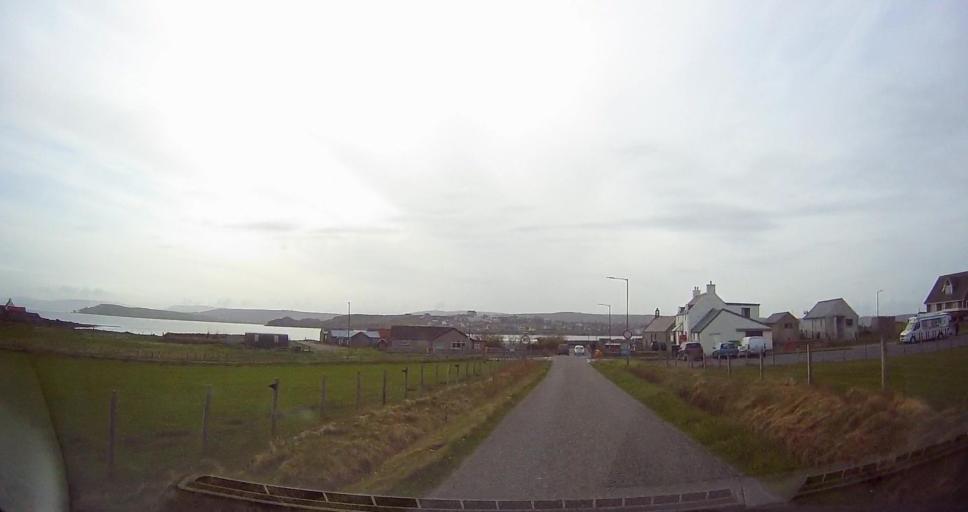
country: GB
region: Scotland
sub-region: Shetland Islands
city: Shetland
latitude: 60.1499
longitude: -1.1099
